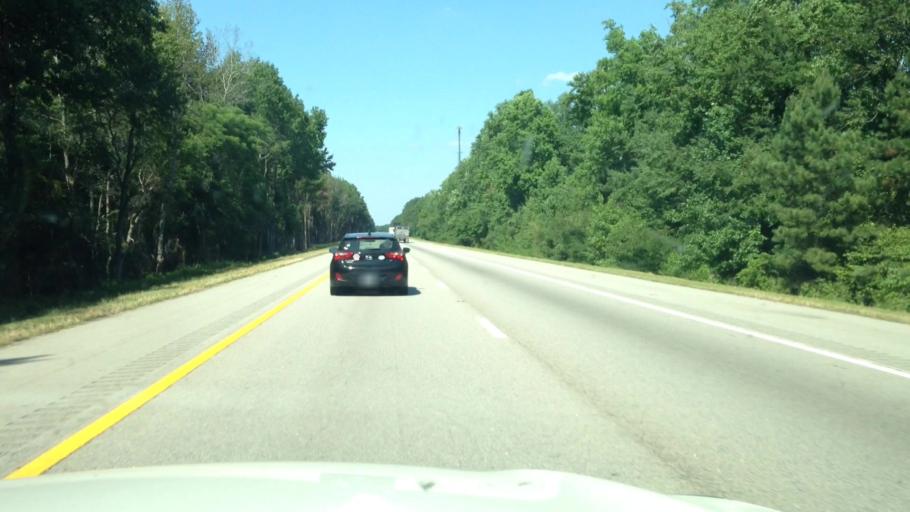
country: US
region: North Carolina
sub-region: Wilson County
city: Lucama
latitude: 35.6736
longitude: -78.0731
